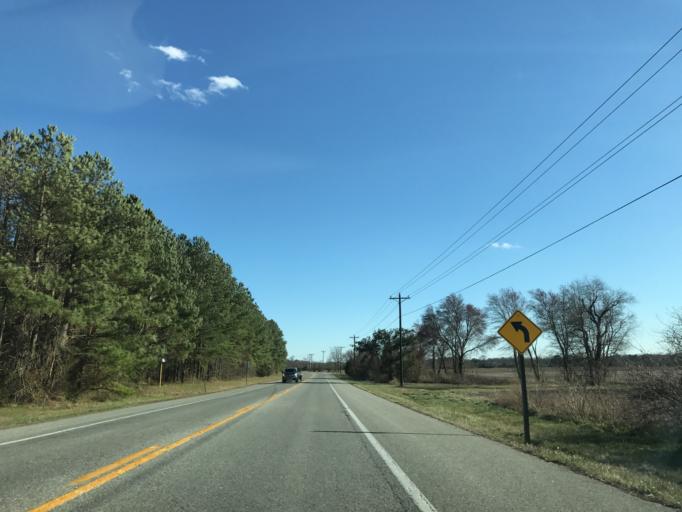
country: US
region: Maryland
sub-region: Caroline County
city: Greensboro
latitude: 39.0636
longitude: -75.8496
